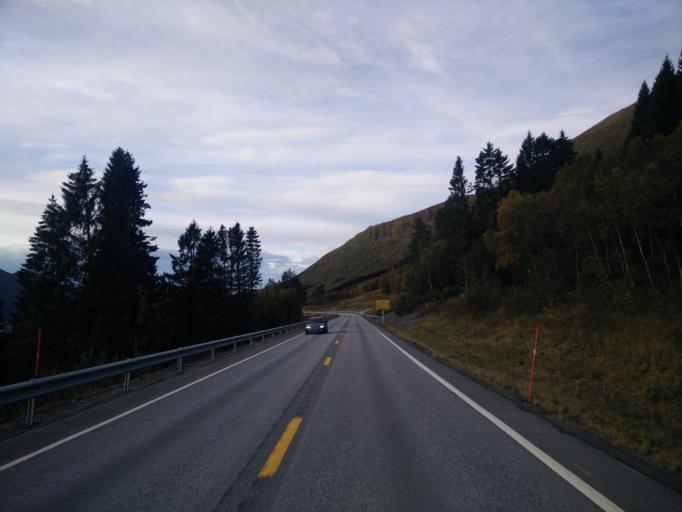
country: NO
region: More og Romsdal
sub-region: Gjemnes
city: Batnfjordsora
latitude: 62.9498
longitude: 7.7572
